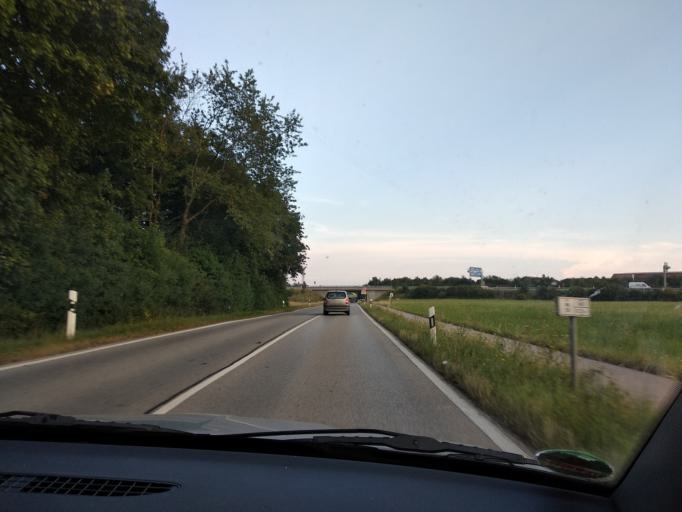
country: DE
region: Bavaria
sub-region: Upper Bavaria
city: Feldkirchen
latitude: 48.1446
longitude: 11.7517
